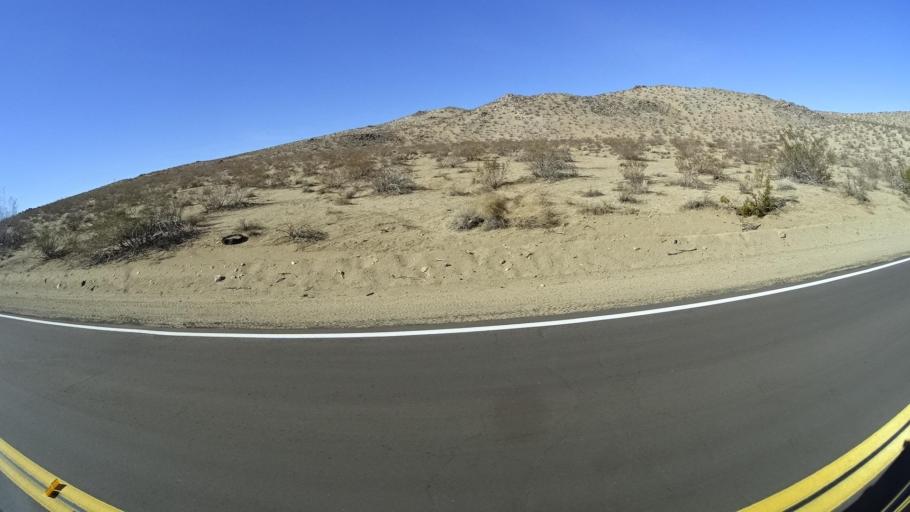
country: US
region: California
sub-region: Kern County
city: Ridgecrest
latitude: 35.5348
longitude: -117.5885
